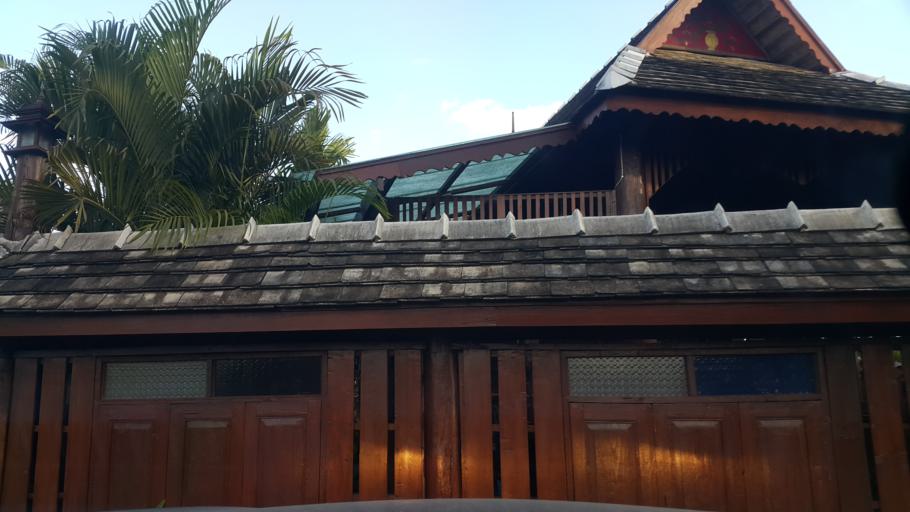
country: TH
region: Chiang Mai
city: Mae On
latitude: 18.7607
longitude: 99.2482
